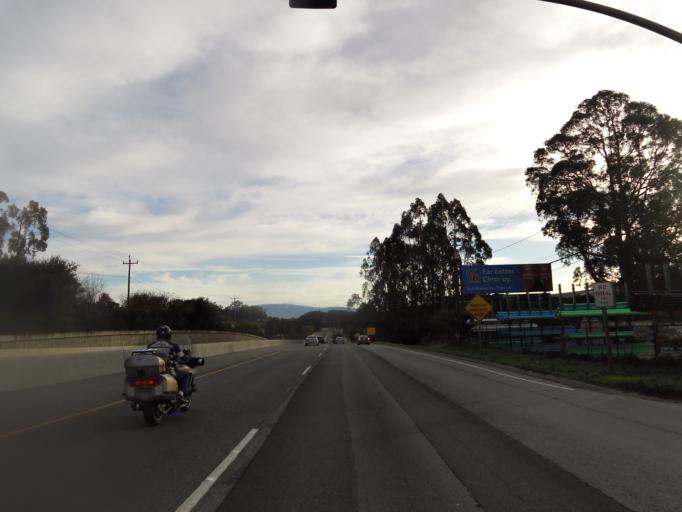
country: US
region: California
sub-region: Monterey County
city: Prunedale
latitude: 36.7759
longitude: -121.6696
